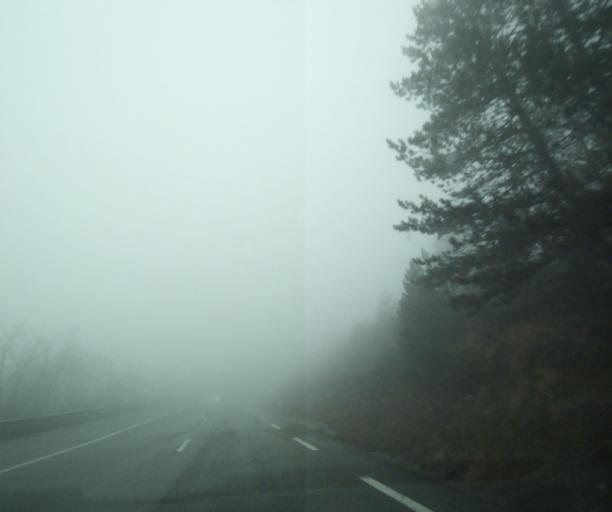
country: FR
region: Rhone-Alpes
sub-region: Departement de l'Ardeche
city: Saint-Priest
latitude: 44.7086
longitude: 4.4883
